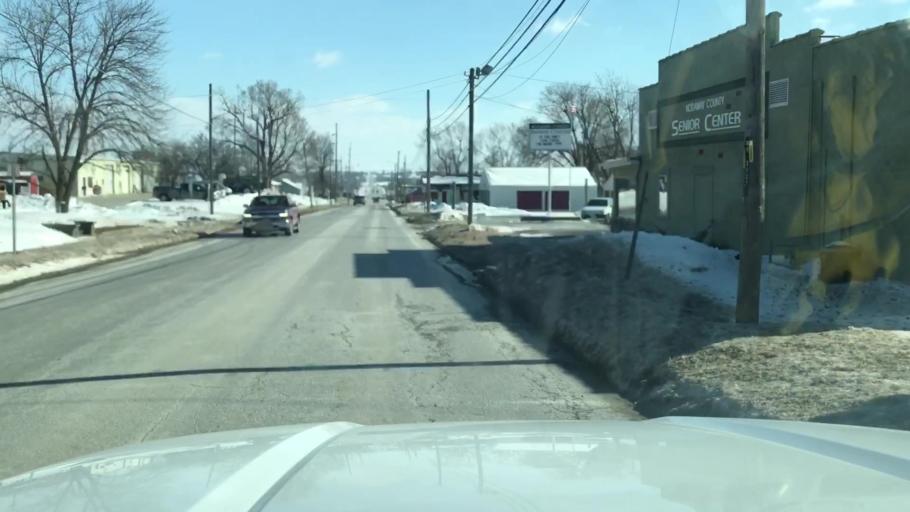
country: US
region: Missouri
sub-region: Nodaway County
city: Maryville
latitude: 40.3454
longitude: -94.8596
